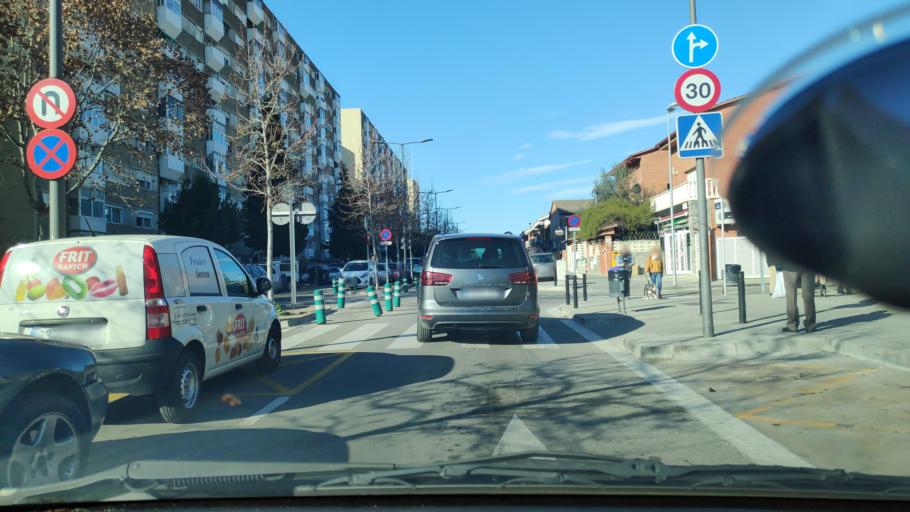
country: ES
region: Catalonia
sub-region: Provincia de Barcelona
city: Barbera del Valles
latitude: 41.5097
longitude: 2.1173
